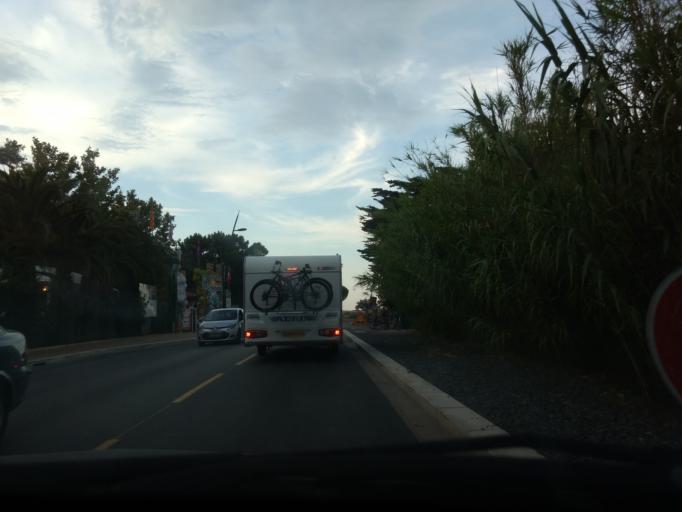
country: FR
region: Languedoc-Roussillon
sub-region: Departement des Pyrenees-Orientales
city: Le Barcares
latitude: 42.7782
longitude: 3.0298
